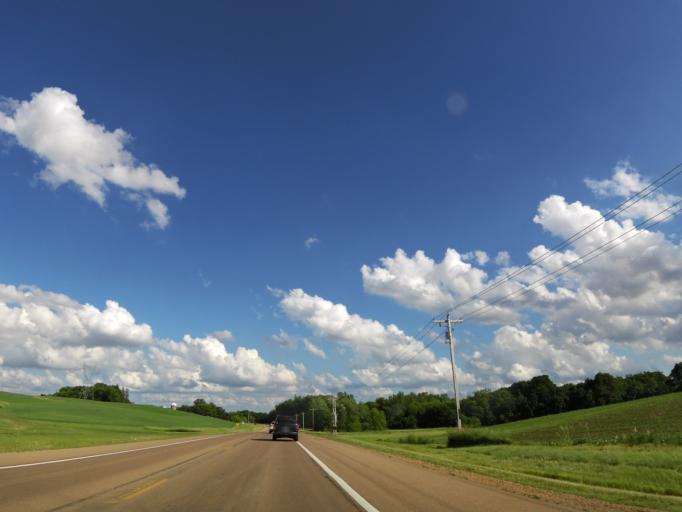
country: US
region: Minnesota
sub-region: Carver County
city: Victoria
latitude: 44.8150
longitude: -93.6845
